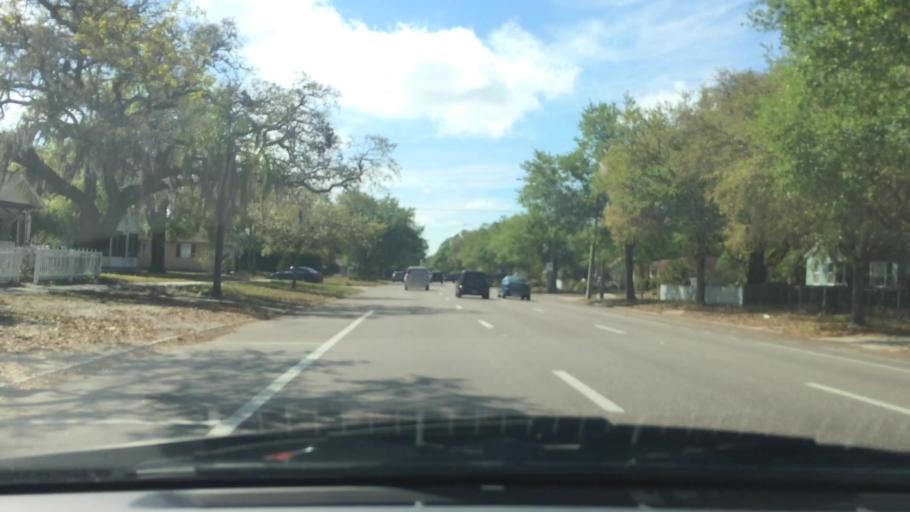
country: US
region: Florida
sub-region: Pinellas County
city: Saint Petersburg
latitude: 27.7719
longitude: -82.6868
